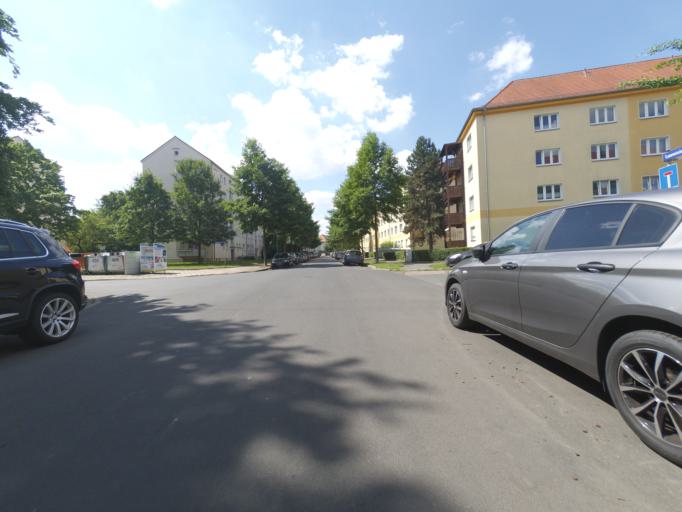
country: DE
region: Saxony
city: Albertstadt
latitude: 51.0365
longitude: 13.7989
